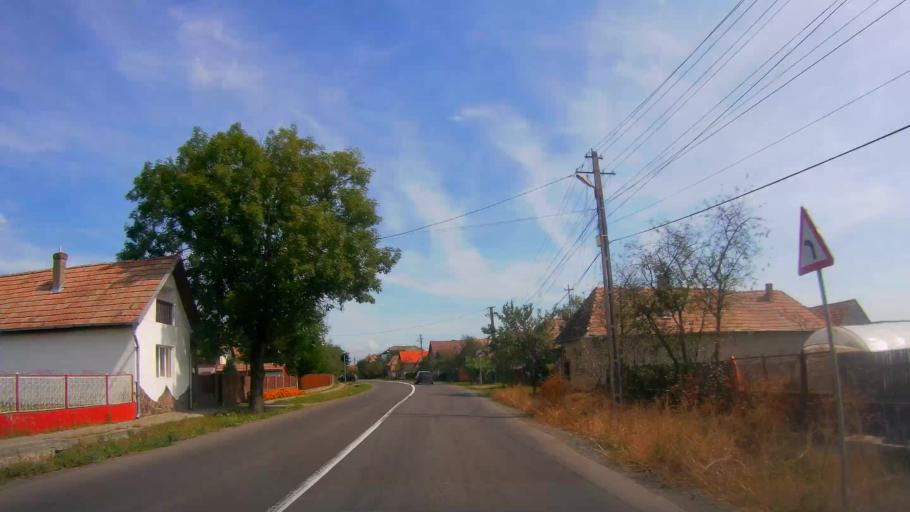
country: RO
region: Mures
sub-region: Comuna Craciunesti
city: Craciunesti
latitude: 46.4715
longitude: 24.5552
